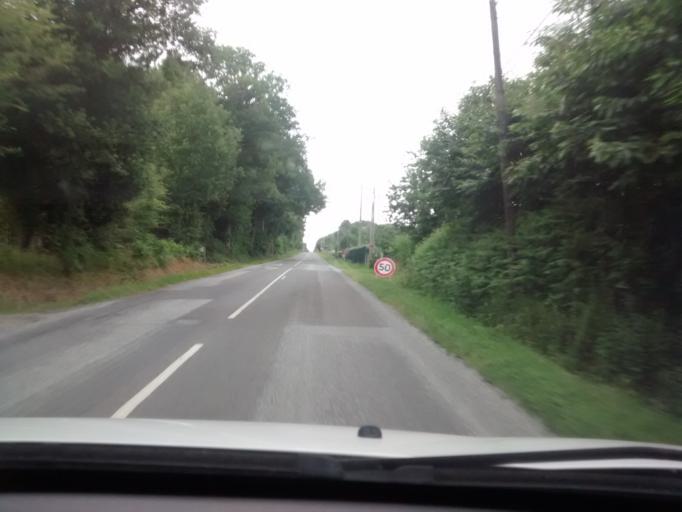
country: FR
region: Brittany
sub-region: Departement d'Ille-et-Vilaine
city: La Bouexiere
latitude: 48.1611
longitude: -1.4406
